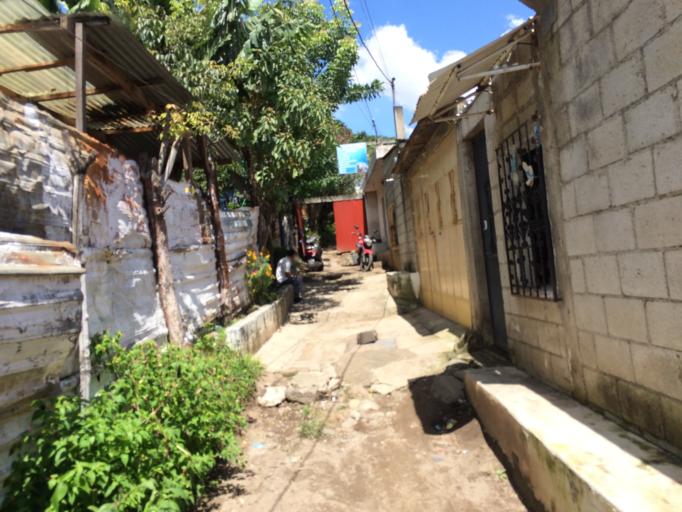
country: GT
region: Guatemala
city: Amatitlan
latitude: 14.4927
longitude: -90.6440
